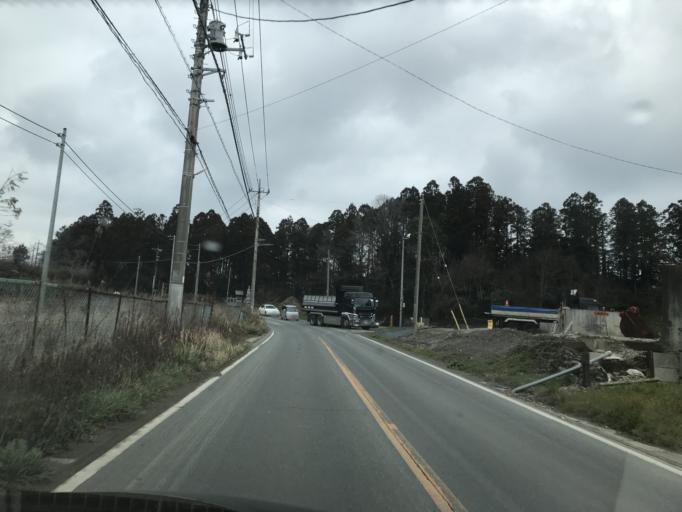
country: JP
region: Chiba
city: Sawara
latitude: 35.8392
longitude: 140.5052
